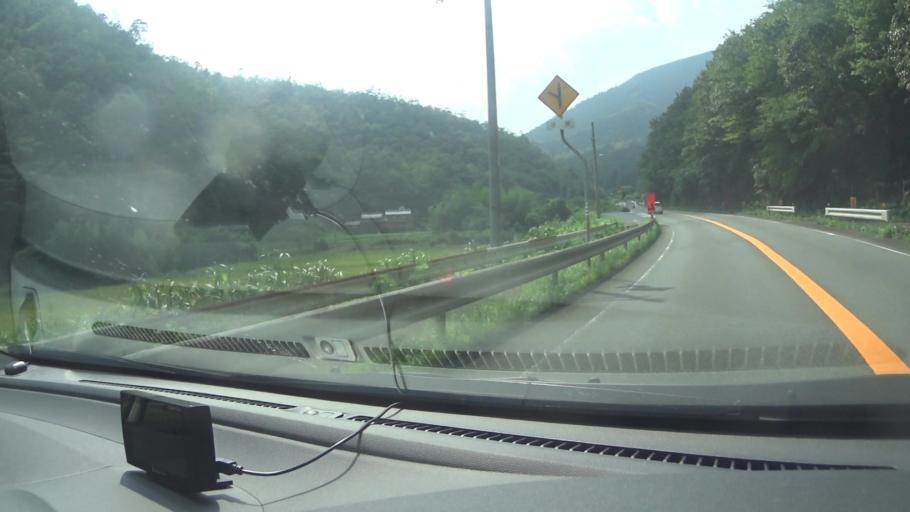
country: JP
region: Hyogo
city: Sasayama
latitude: 35.1479
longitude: 135.3544
